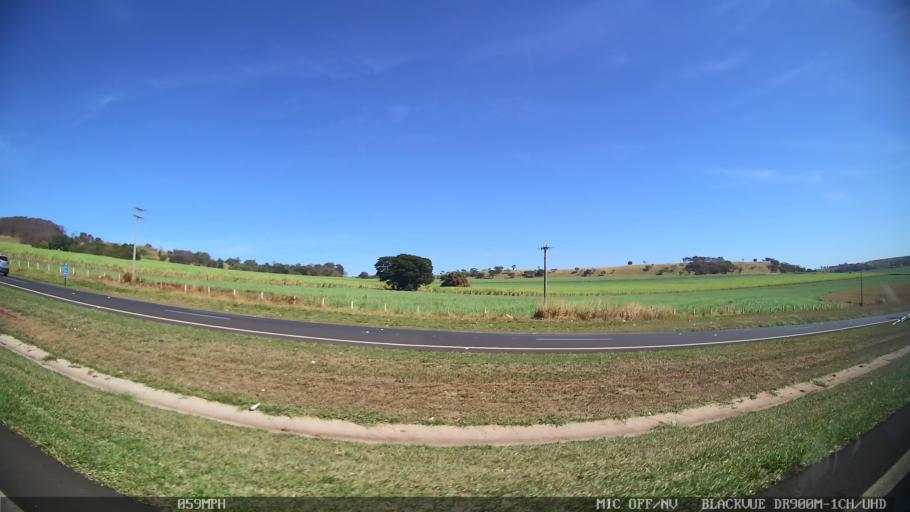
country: BR
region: Sao Paulo
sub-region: Cravinhos
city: Cravinhos
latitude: -21.4214
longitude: -47.6588
